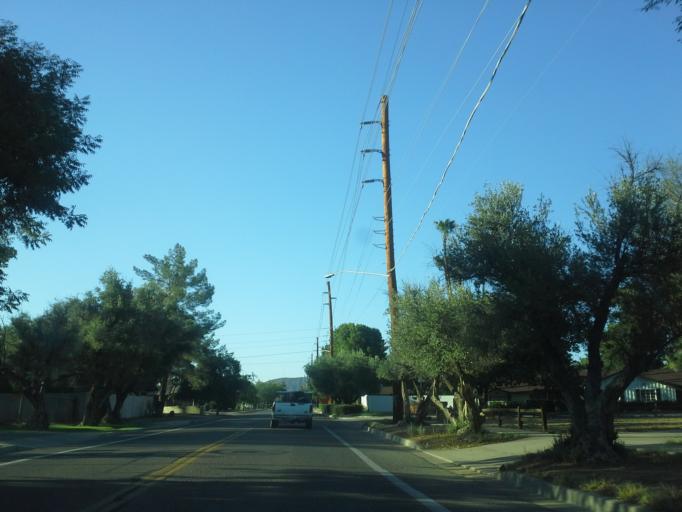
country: US
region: Arizona
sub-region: Maricopa County
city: Glendale
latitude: 33.5484
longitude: -112.0912
